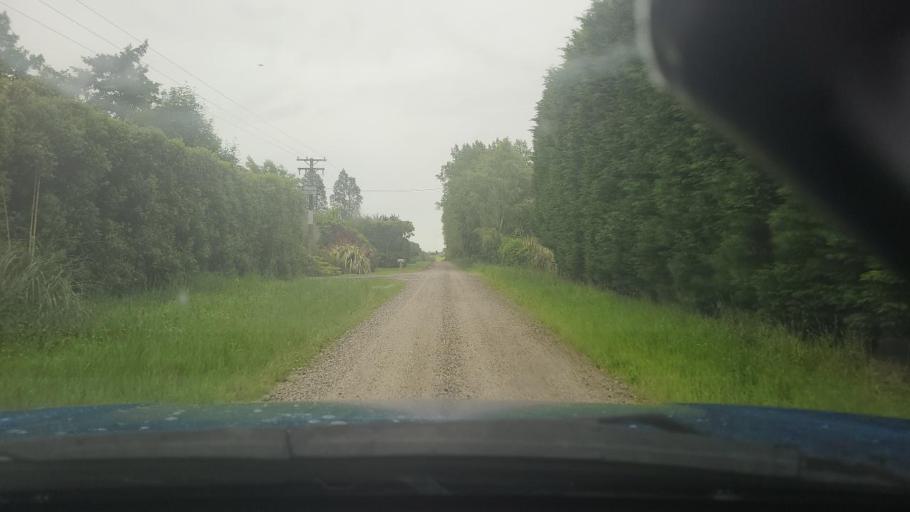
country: NZ
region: Southland
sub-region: Invercargill City
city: Invercargill
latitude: -46.3708
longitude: 168.5635
